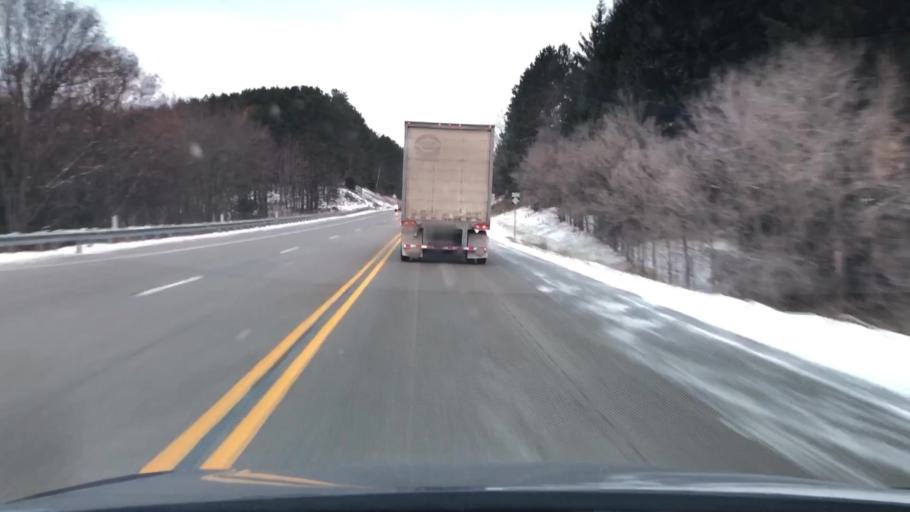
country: US
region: Michigan
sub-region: Wexford County
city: Cadillac
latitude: 44.1797
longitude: -85.3806
